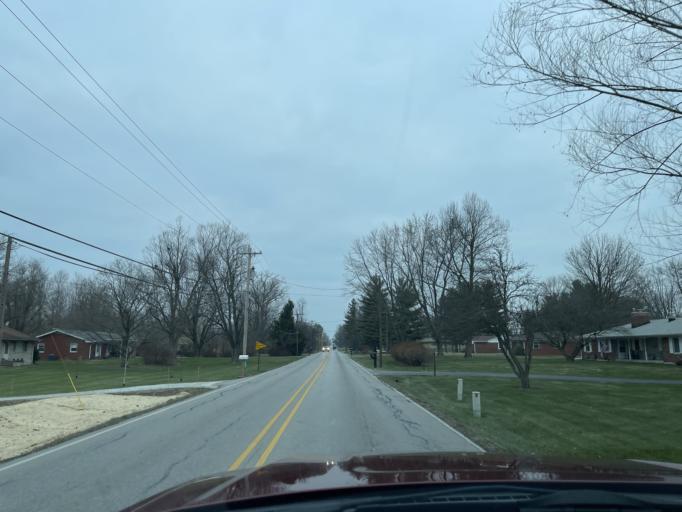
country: US
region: Indiana
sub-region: Hendricks County
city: Avon
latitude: 39.7895
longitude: -86.4003
